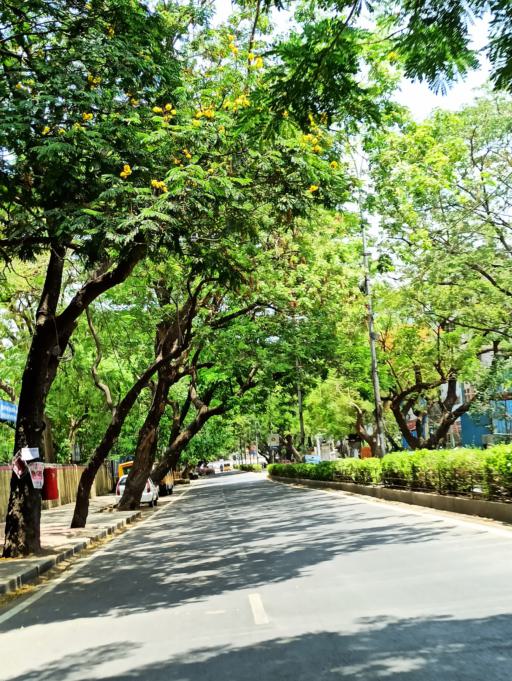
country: IN
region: Tamil Nadu
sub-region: Chennai
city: Chetput
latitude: 13.0828
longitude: 80.2012
